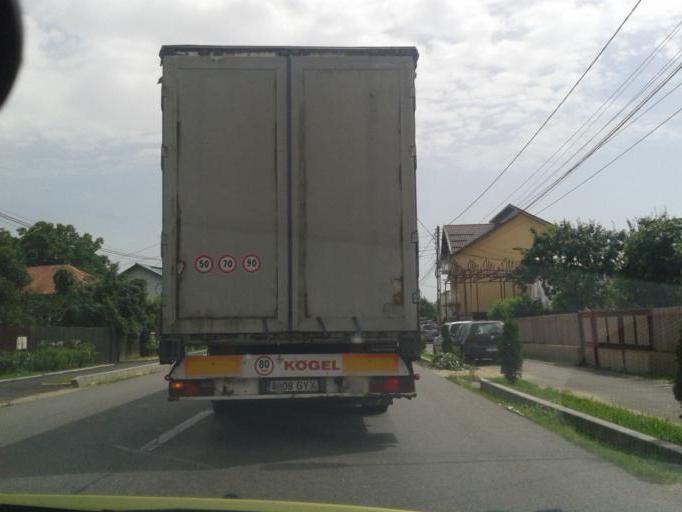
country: RO
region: Dambovita
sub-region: Oras Gaesti
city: Gaesti
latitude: 44.7206
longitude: 25.3296
